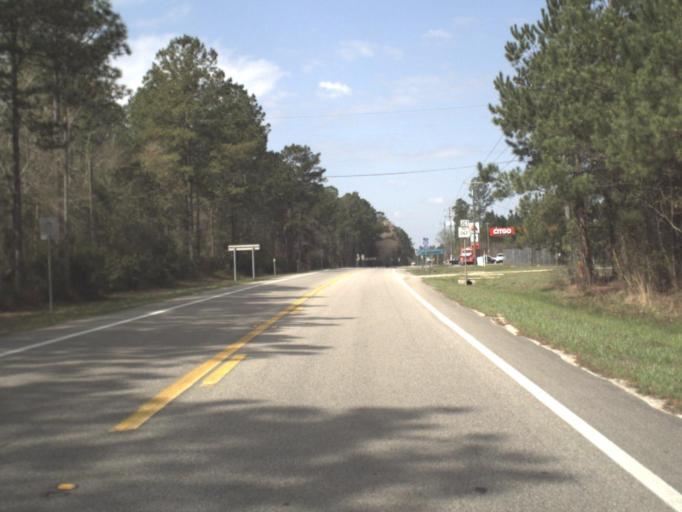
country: US
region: Florida
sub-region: Gadsden County
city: Quincy
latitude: 30.3881
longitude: -84.6823
